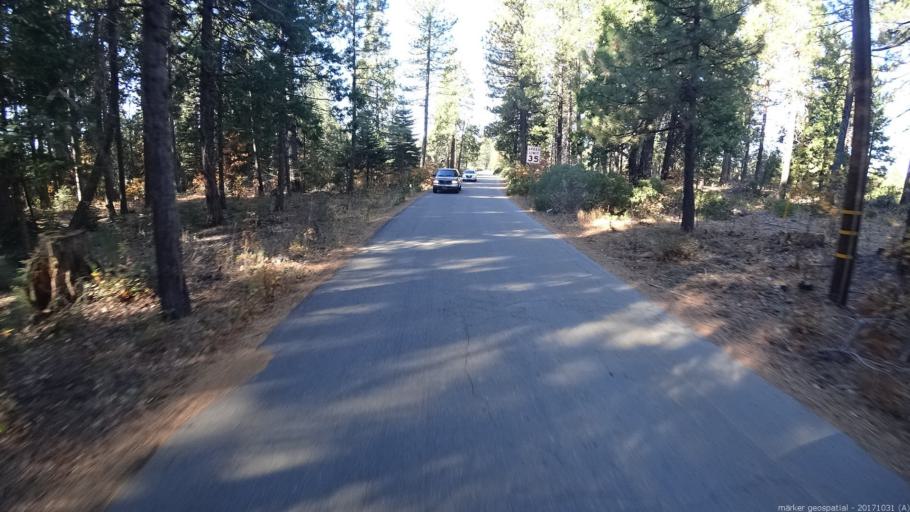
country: US
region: California
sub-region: Shasta County
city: Shingletown
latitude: 40.5179
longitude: -121.8183
